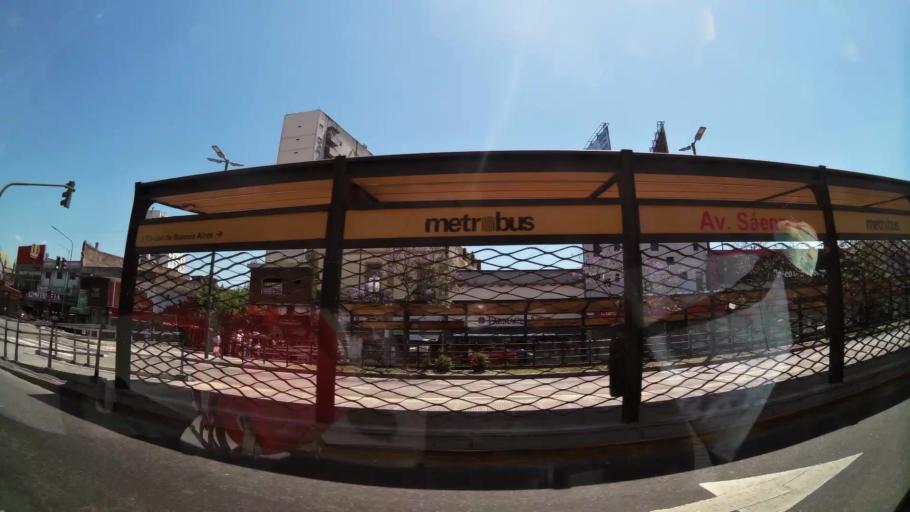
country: AR
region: Buenos Aires
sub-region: Partido de Avellaneda
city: Avellaneda
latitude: -34.6506
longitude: -58.4161
